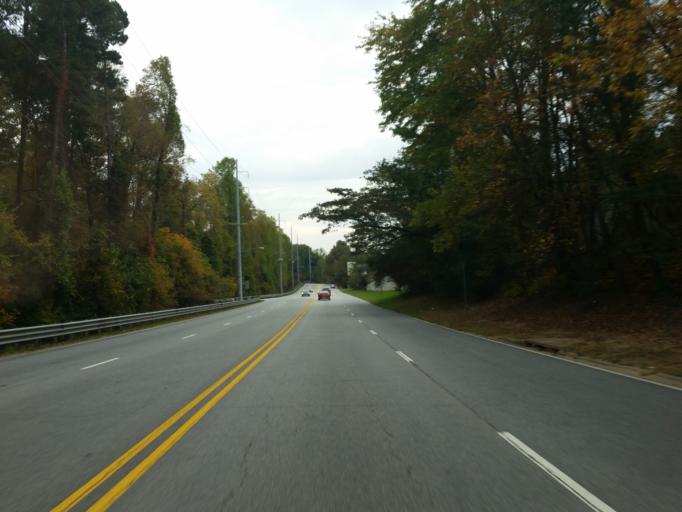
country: US
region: Georgia
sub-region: Cobb County
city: Vinings
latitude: 33.8598
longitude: -84.4344
